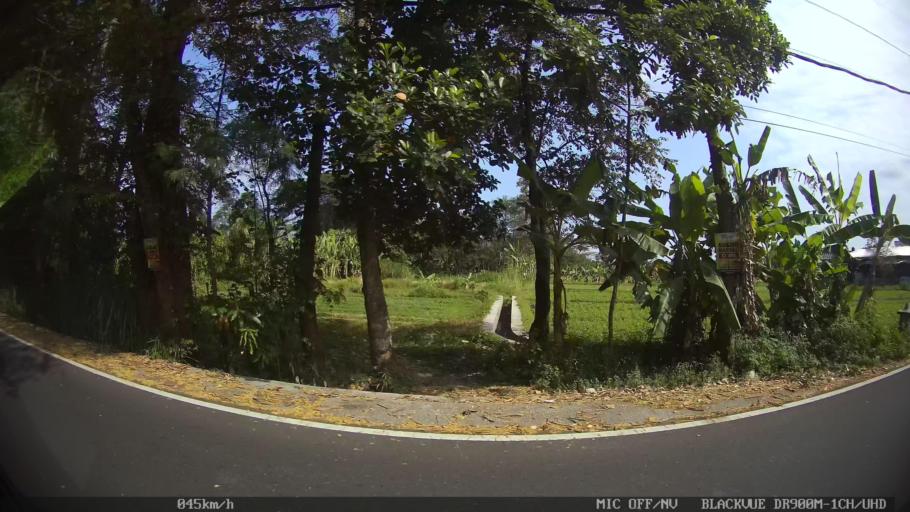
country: ID
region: Daerah Istimewa Yogyakarta
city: Depok
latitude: -7.7279
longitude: 110.4278
